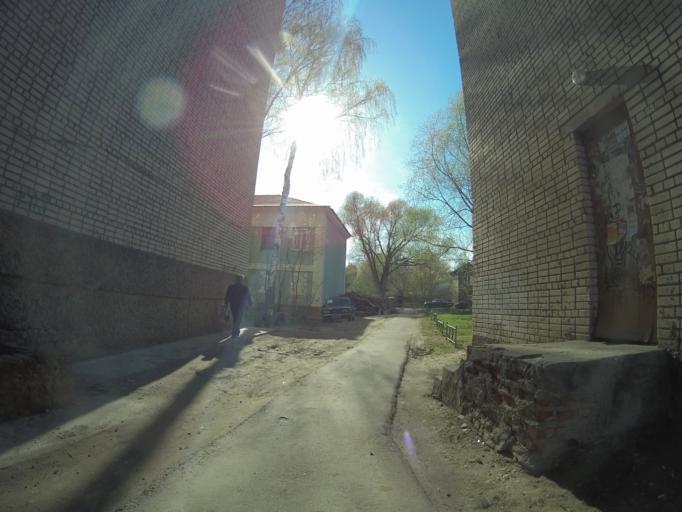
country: RU
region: Vladimir
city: Vladimir
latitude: 56.1483
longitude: 40.4216
